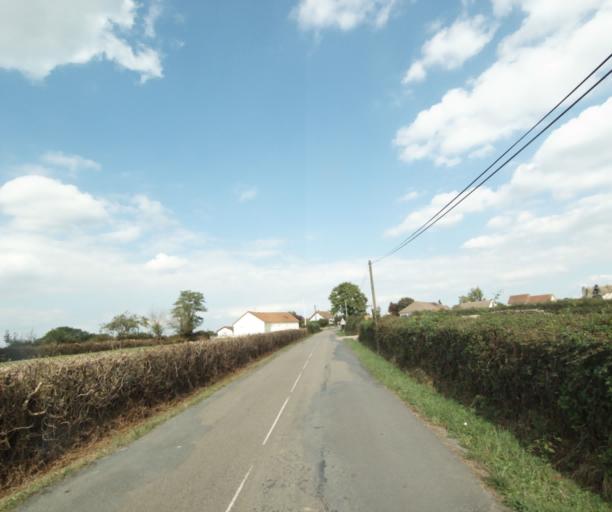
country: FR
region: Bourgogne
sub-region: Departement de Saone-et-Loire
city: Palinges
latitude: 46.4968
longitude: 4.2194
